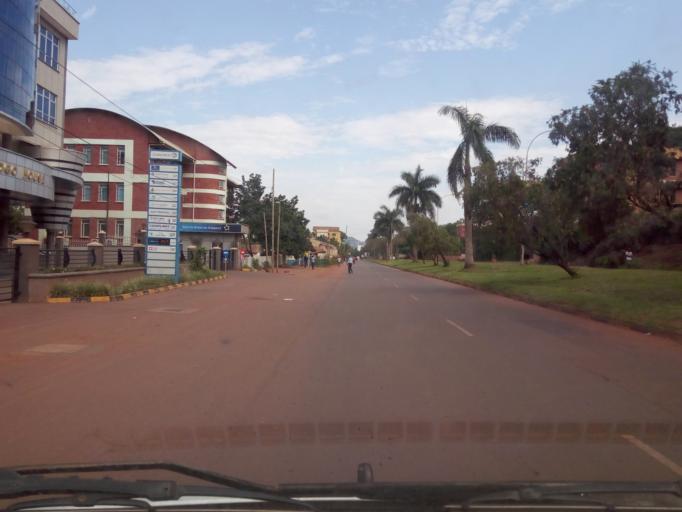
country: UG
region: Central Region
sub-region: Kampala District
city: Kampala
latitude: 0.3343
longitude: 32.6018
